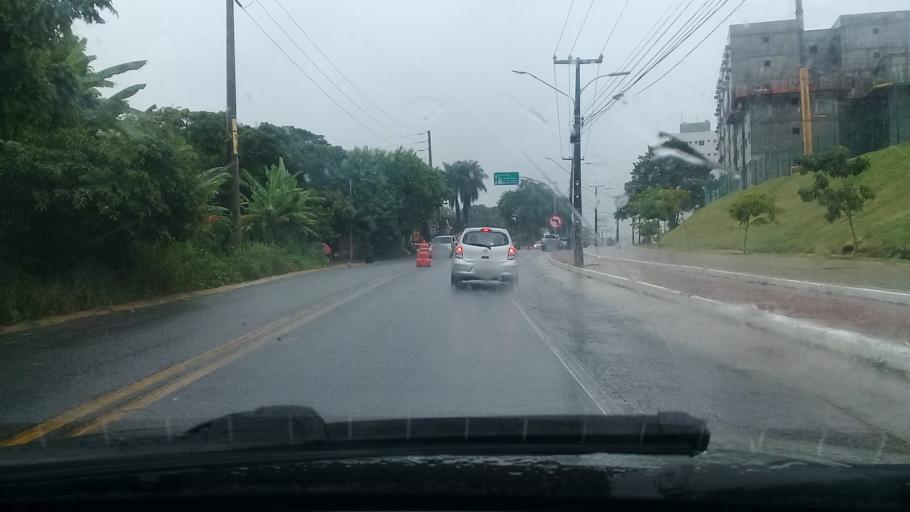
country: BR
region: Pernambuco
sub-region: Paulista
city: Paulista
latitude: -7.9485
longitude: -34.8871
